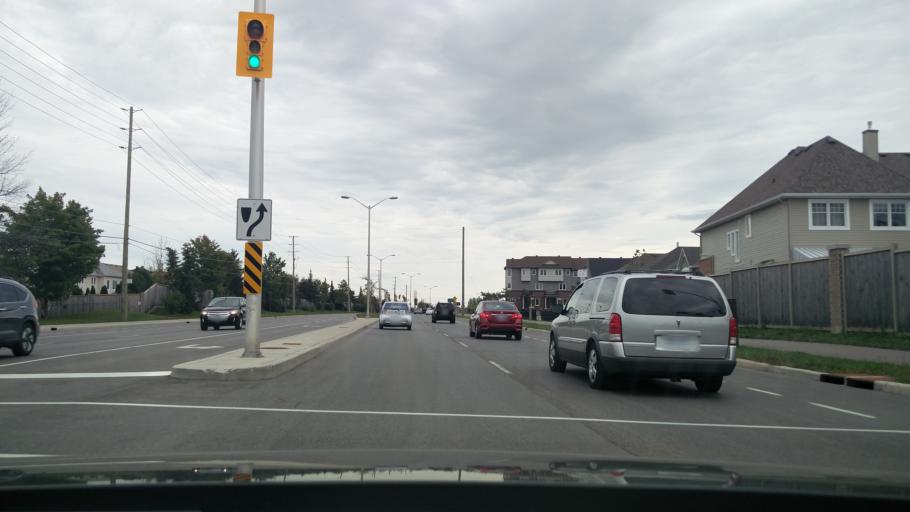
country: CA
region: Ontario
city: Bells Corners
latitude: 45.2592
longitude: -75.7309
